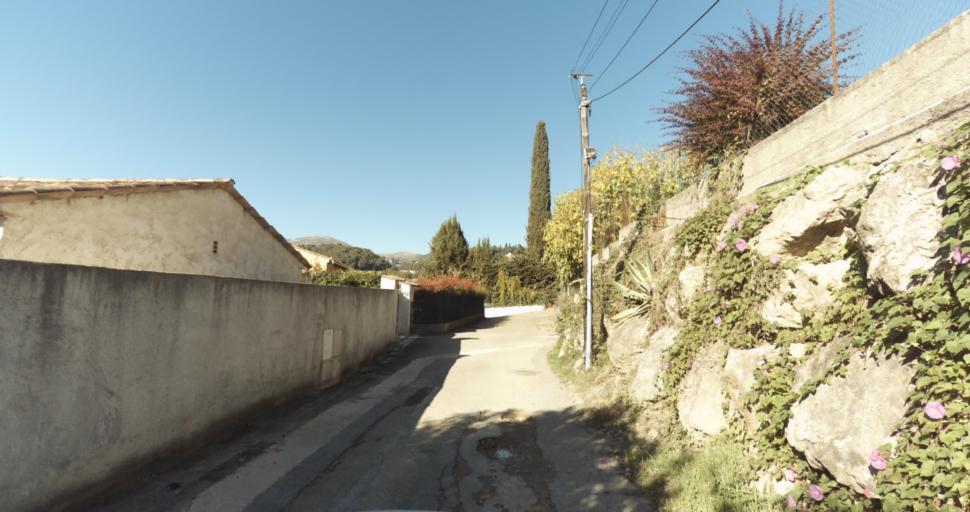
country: FR
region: Provence-Alpes-Cote d'Azur
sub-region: Departement des Alpes-Maritimes
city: Saint-Paul-de-Vence
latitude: 43.7084
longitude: 7.1270
